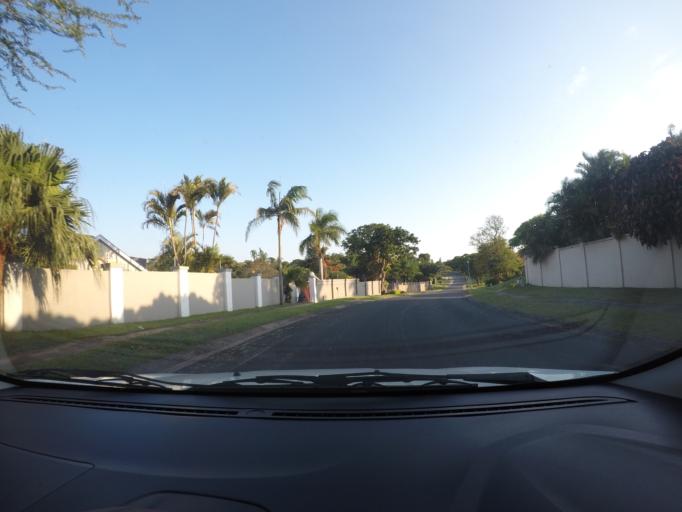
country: ZA
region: KwaZulu-Natal
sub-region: uThungulu District Municipality
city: Richards Bay
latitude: -28.7825
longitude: 32.0931
